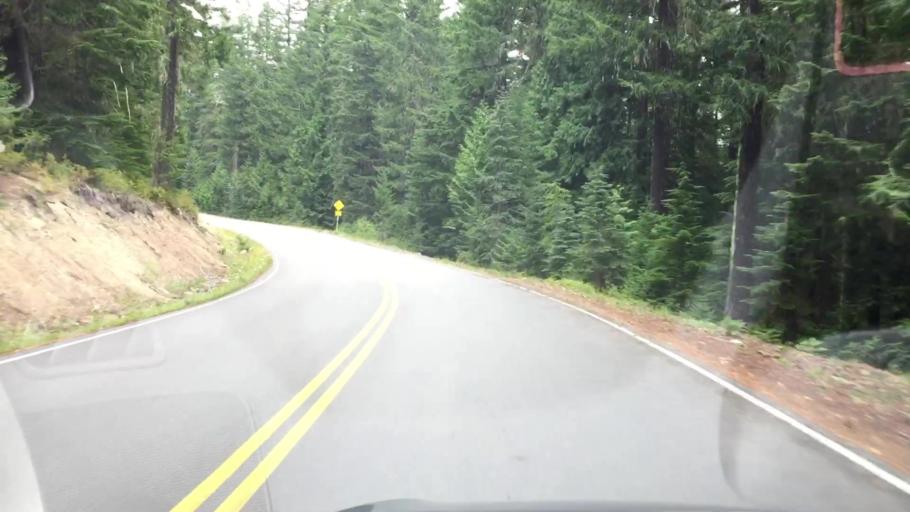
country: US
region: Washington
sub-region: Klickitat County
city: White Salmon
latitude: 46.1442
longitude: -121.6273
